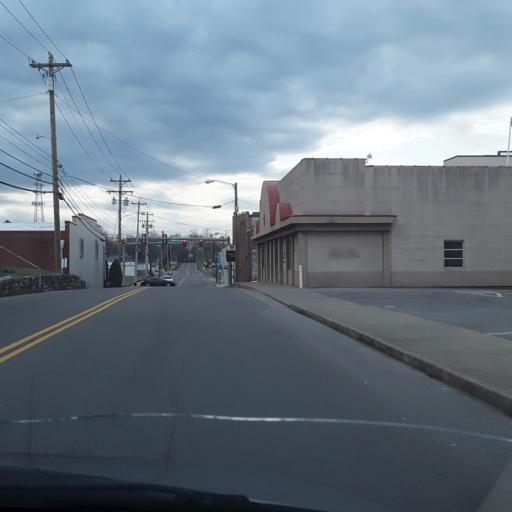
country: US
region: Tennessee
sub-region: Wilson County
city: Lebanon
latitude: 36.2068
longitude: -86.2901
